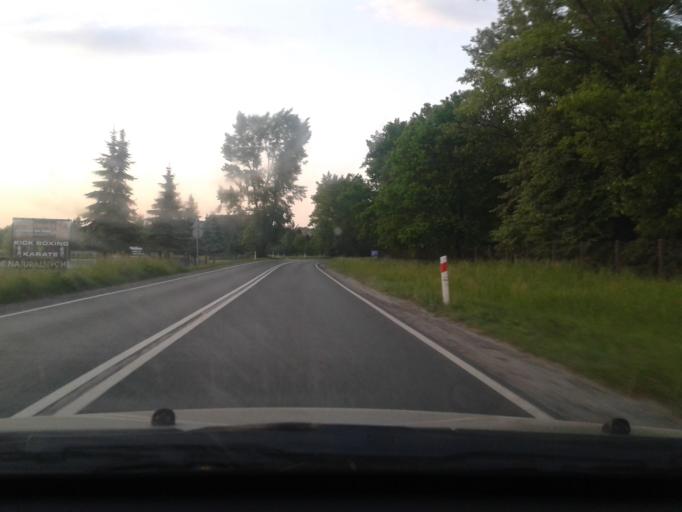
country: PL
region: Lesser Poland Voivodeship
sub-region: Powiat oswiecimski
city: Rajsko
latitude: 50.0195
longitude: 19.1972
